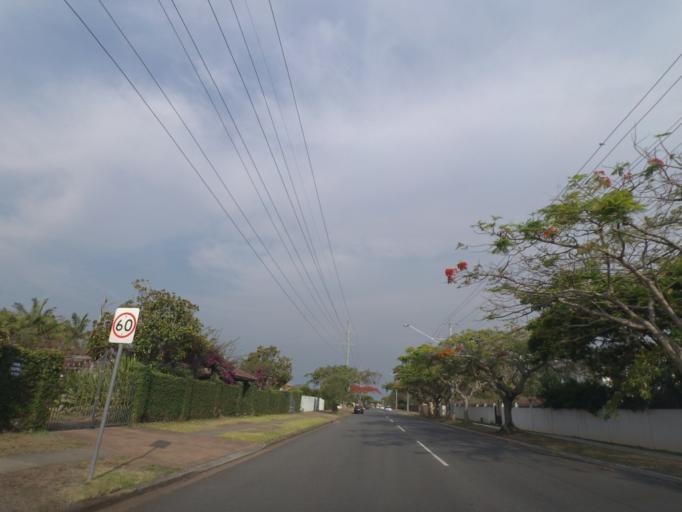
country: AU
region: Queensland
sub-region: Brisbane
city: Robertson
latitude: -27.5662
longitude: 153.0604
